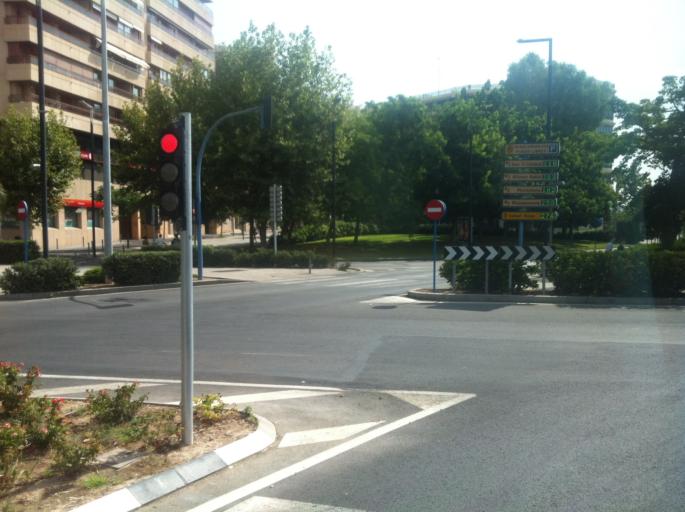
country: ES
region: Valencia
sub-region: Provincia de Alicante
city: Alicante
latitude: 38.3385
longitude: -0.4936
